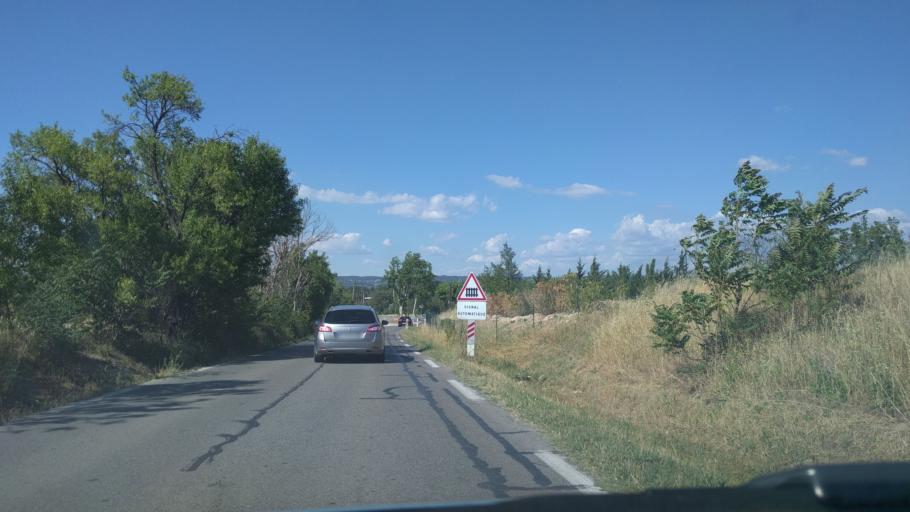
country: FR
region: Provence-Alpes-Cote d'Azur
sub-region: Departement des Bouches-du-Rhone
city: Cabries
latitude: 43.4987
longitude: 5.3496
